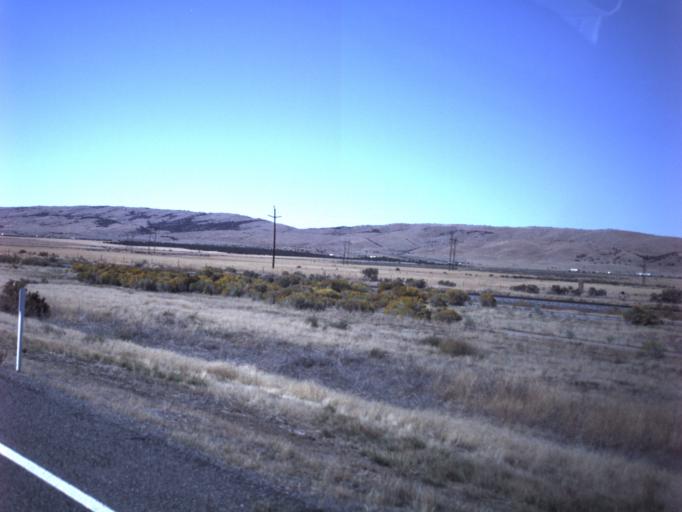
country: US
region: Utah
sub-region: Juab County
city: Nephi
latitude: 39.5563
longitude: -111.9201
